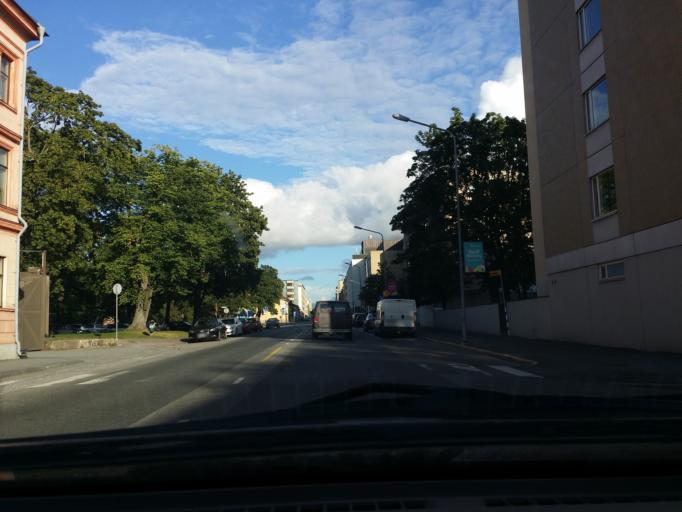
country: FI
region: Satakunta
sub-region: Pori
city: Pori
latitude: 61.4885
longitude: 21.7911
